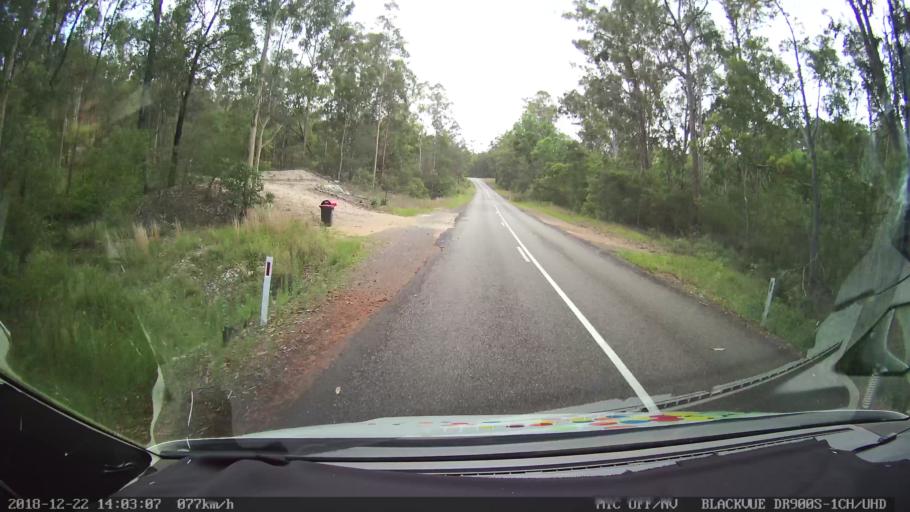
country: AU
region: New South Wales
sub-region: Clarence Valley
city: Coutts Crossing
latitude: -29.9275
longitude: 152.7417
